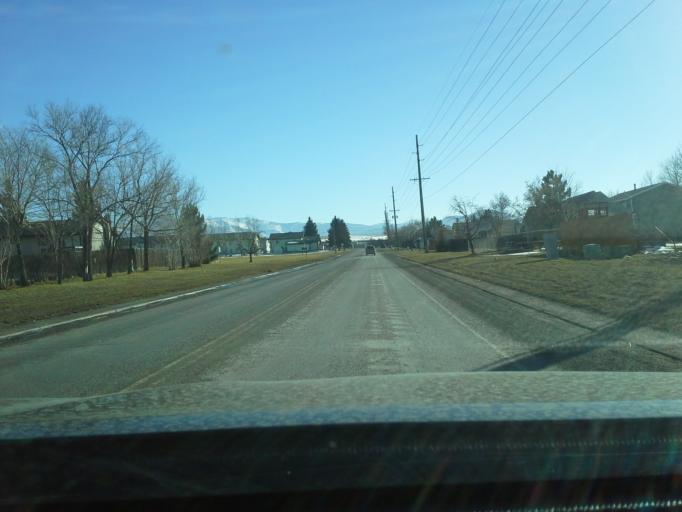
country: US
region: Montana
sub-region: Lewis and Clark County
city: East Helena
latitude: 46.5914
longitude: -111.8939
